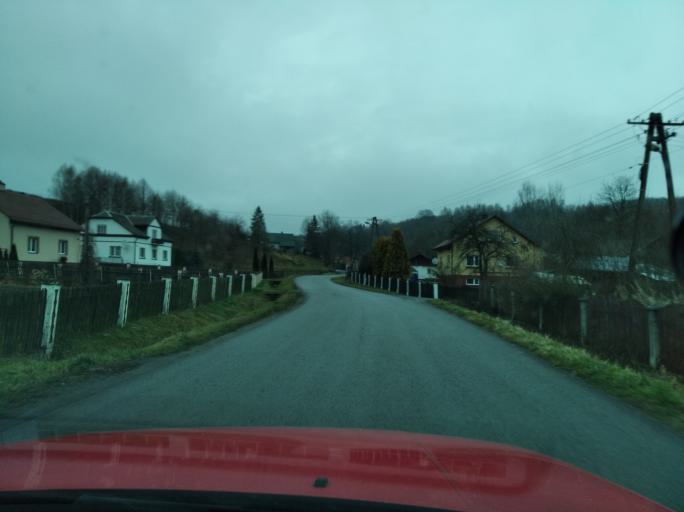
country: PL
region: Subcarpathian Voivodeship
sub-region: Powiat przemyski
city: Nienadowa
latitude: 49.8475
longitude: 22.4297
